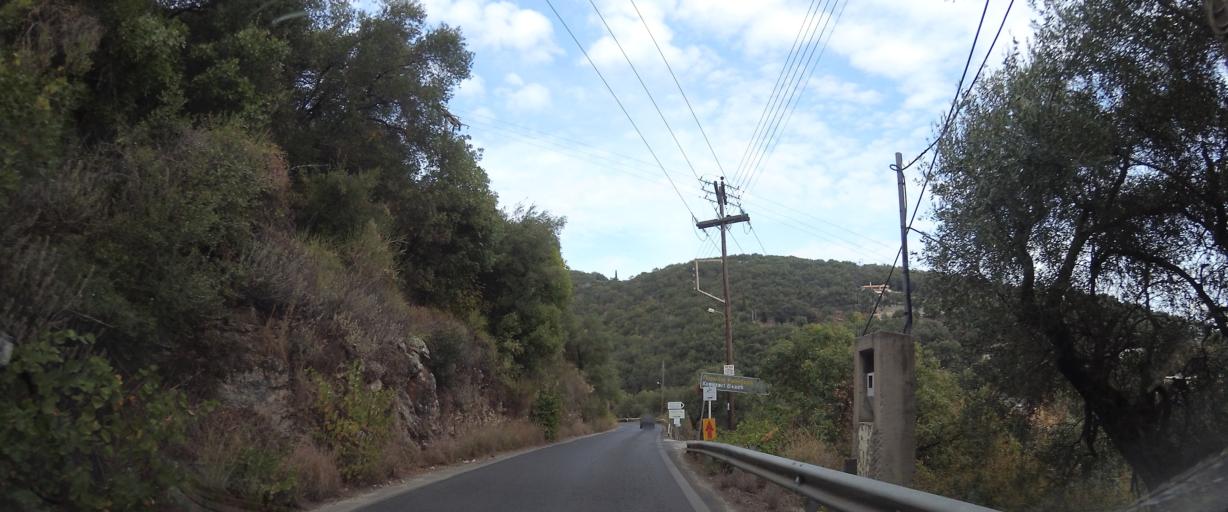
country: GR
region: Ionian Islands
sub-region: Nomos Kerkyras
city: Kontokali
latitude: 39.7332
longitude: 19.9187
